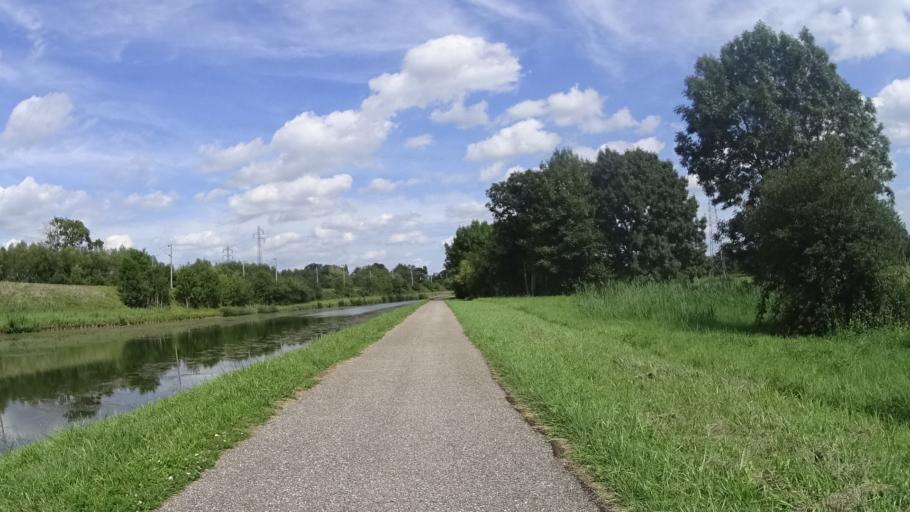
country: FR
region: Lorraine
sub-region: Departement de Meurthe-et-Moselle
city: Ecrouves
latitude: 48.6772
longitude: 5.8468
